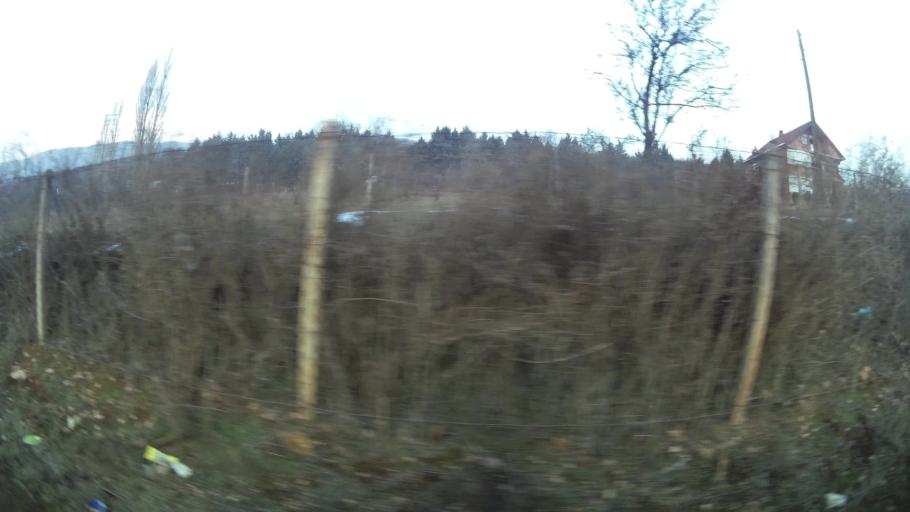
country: MK
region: Aracinovo
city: Arachinovo
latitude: 42.0325
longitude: 21.5547
